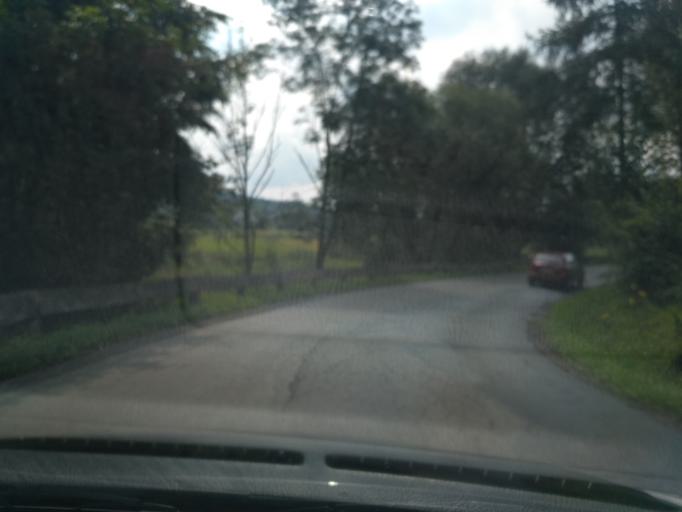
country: PL
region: Subcarpathian Voivodeship
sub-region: Powiat strzyzowski
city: Strzyzow
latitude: 49.8933
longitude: 21.8252
